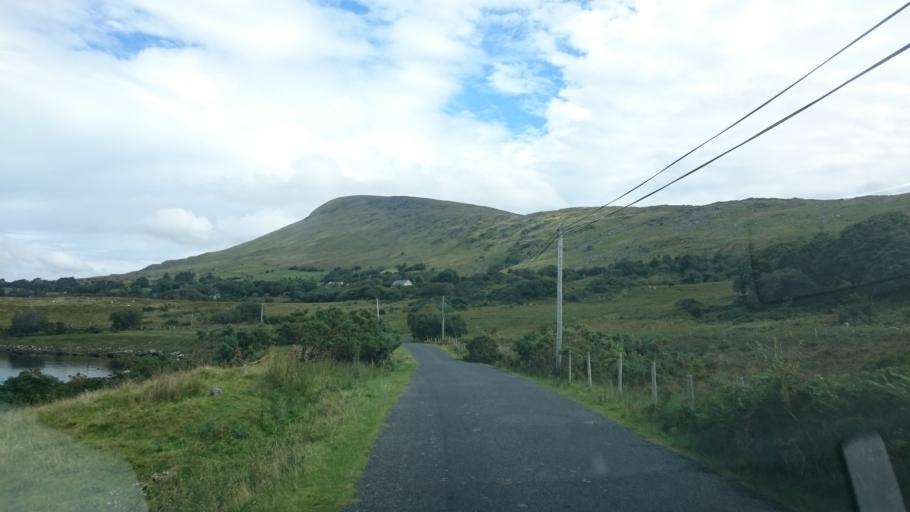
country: IE
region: Connaught
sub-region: Maigh Eo
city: Westport
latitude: 53.9323
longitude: -9.5639
